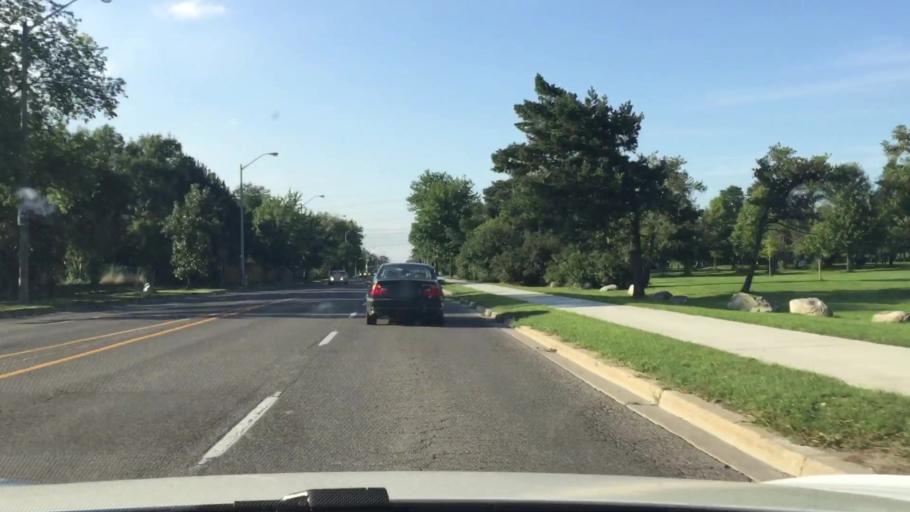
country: CA
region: Ontario
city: Scarborough
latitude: 43.8046
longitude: -79.3093
